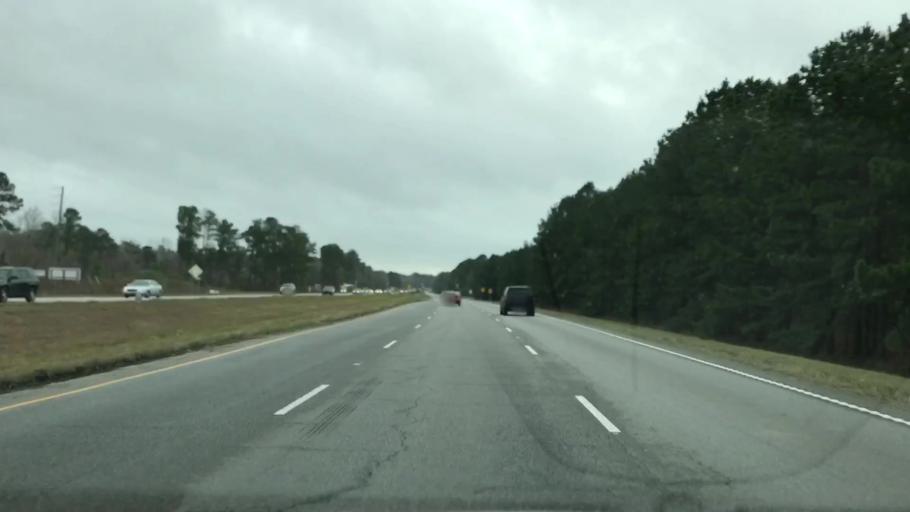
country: US
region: South Carolina
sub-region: Berkeley County
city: Goose Creek
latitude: 33.0584
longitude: -80.0353
